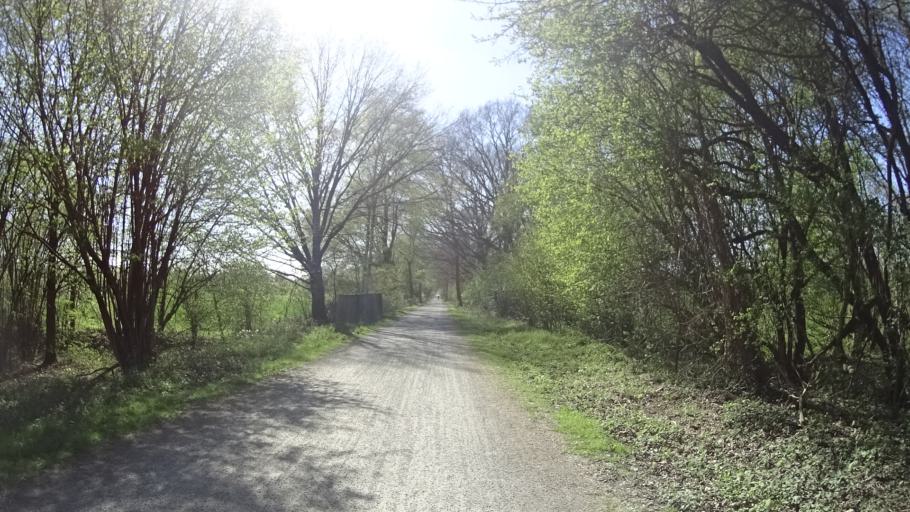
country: DE
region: North Rhine-Westphalia
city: Marl
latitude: 51.7127
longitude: 7.1122
